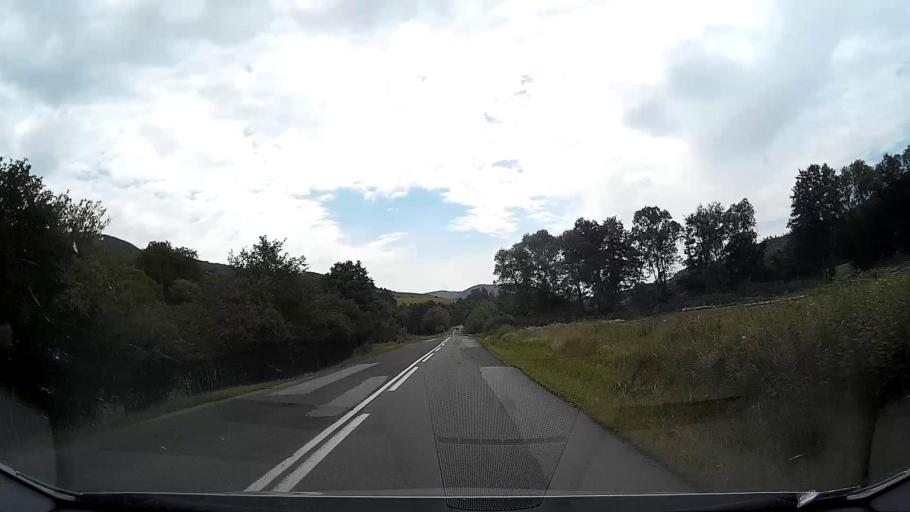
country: SK
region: Banskobystricky
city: Tisovec
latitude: 48.6316
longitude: 19.9507
